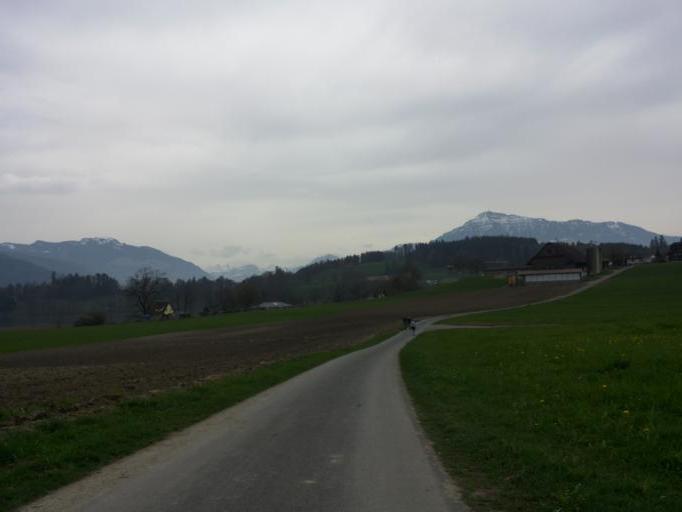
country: CH
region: Lucerne
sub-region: Lucerne-Land District
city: Meierskappel
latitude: 47.1472
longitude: 8.4556
